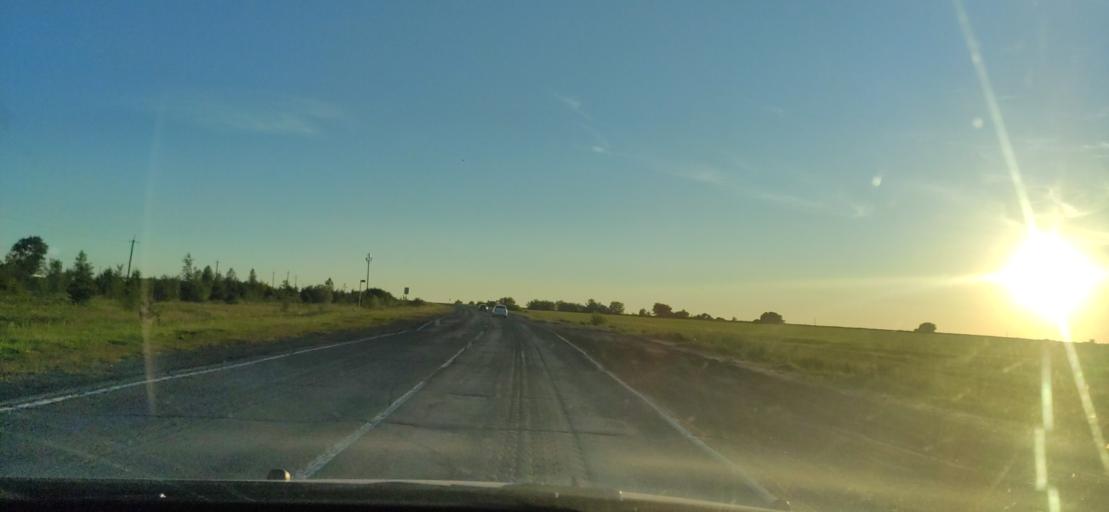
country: RU
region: Ulyanovsk
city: Cherdakly
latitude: 54.3852
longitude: 48.8410
